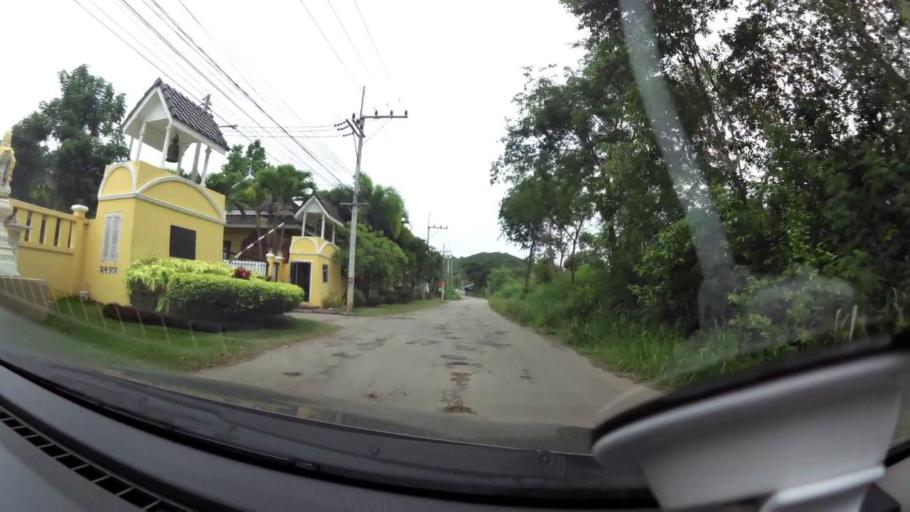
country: TH
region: Prachuap Khiri Khan
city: Pran Buri
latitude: 12.4461
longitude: 99.9708
